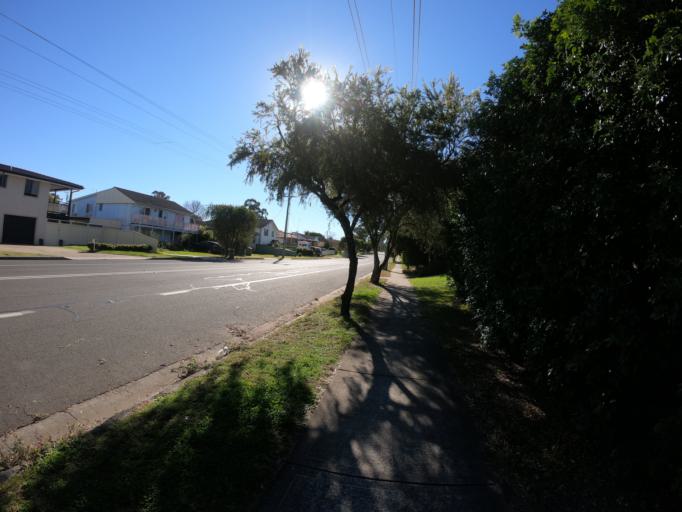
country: AU
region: New South Wales
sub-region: Hawkesbury
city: South Windsor
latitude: -33.6290
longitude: 150.7982
